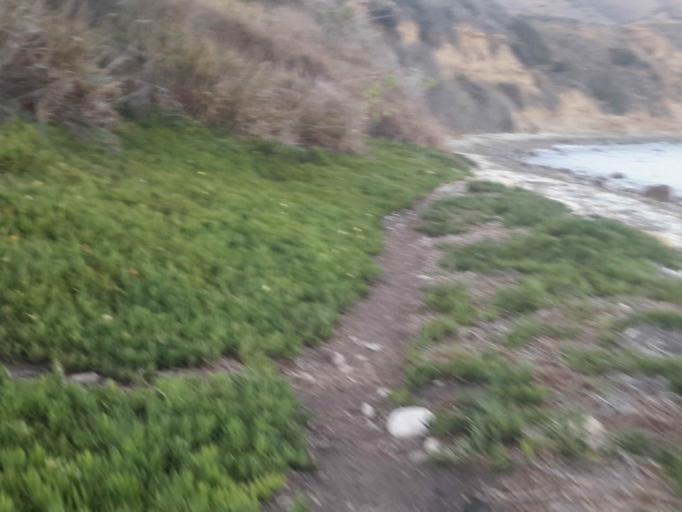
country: US
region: California
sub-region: Santa Barbara County
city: Santa Ynez
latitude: 34.4593
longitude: -120.0212
